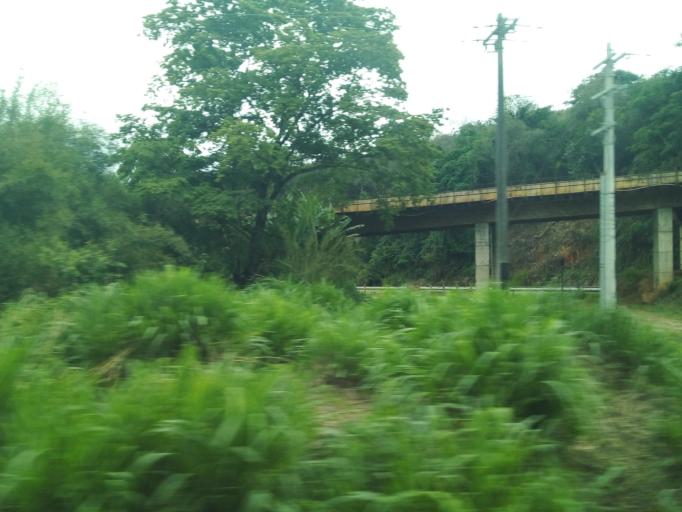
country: BR
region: Minas Gerais
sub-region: Nova Era
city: Nova Era
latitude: -19.7436
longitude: -43.0206
